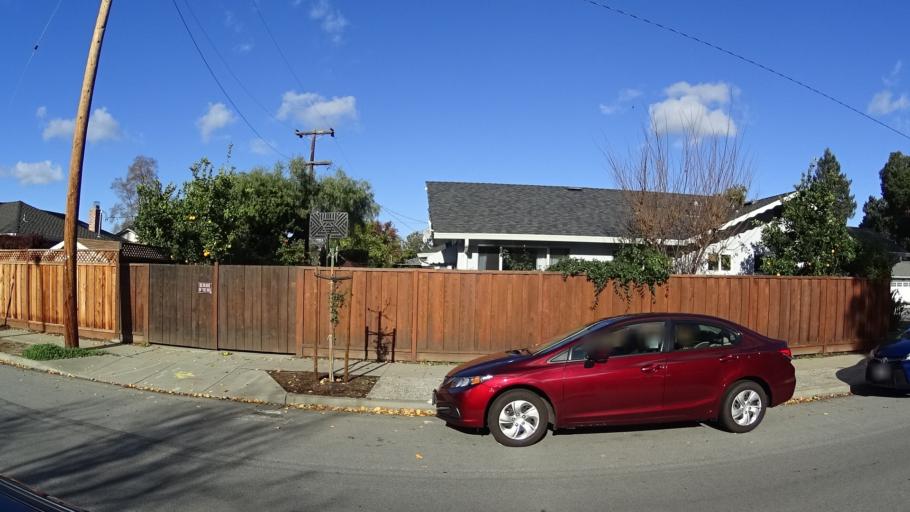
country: US
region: California
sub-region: Santa Clara County
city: Sunnyvale
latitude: 37.3714
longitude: -122.0418
